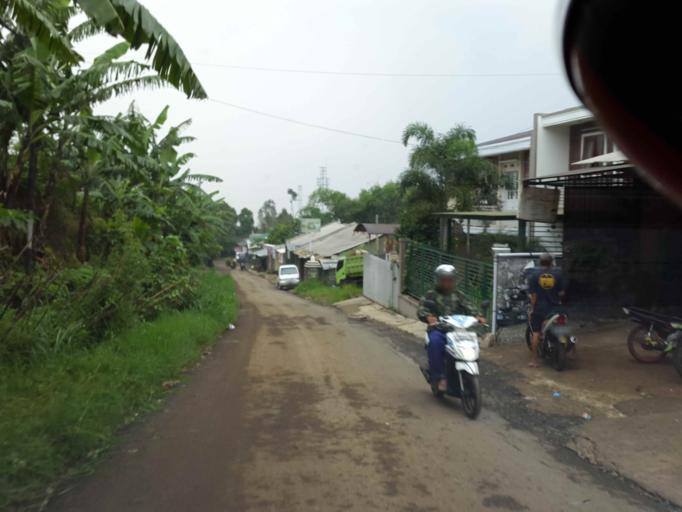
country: ID
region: West Java
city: Cimahi
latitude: -6.8464
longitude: 107.5824
